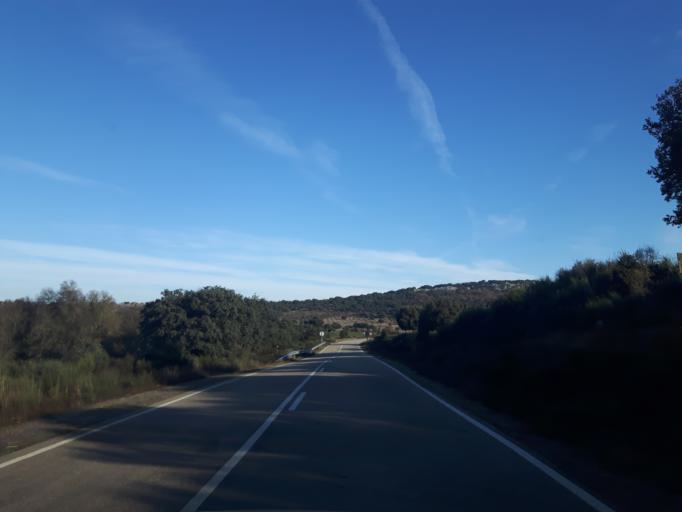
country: ES
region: Castille and Leon
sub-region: Provincia de Salamanca
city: Olmedo de Camaces
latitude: 40.8888
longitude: -6.6235
